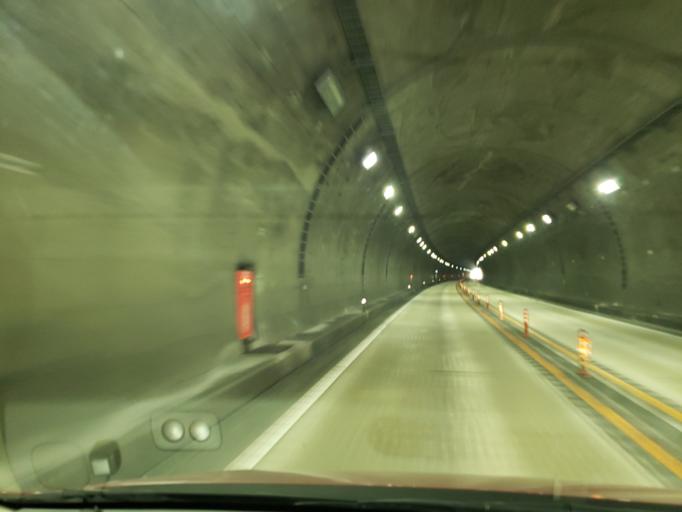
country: JP
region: Tokushima
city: Kamojimacho-jogejima
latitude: 34.1055
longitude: 134.2937
